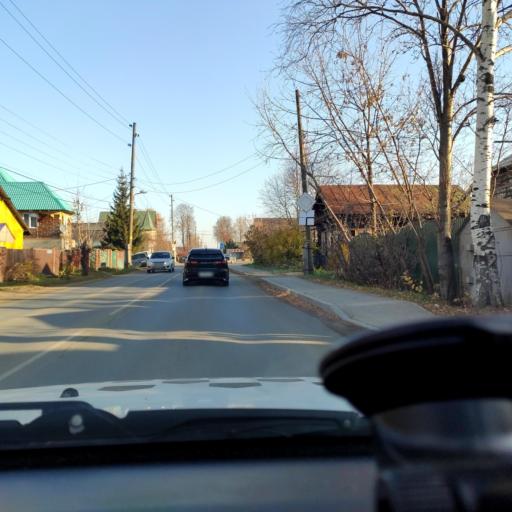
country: RU
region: Perm
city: Perm
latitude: 58.0489
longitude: 56.3330
